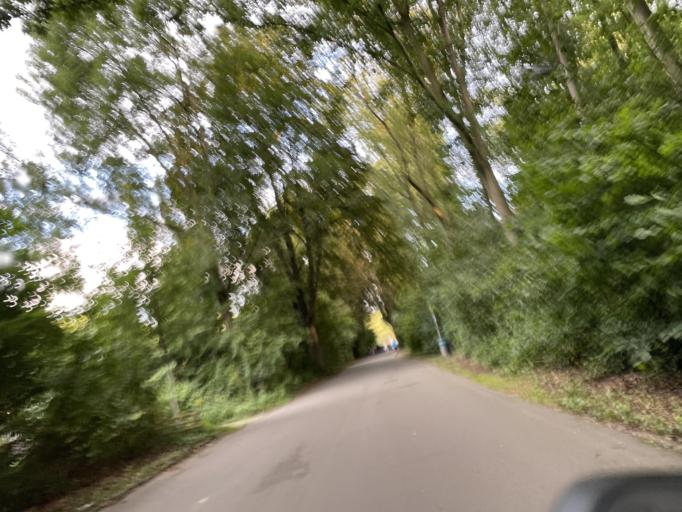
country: DE
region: North Rhine-Westphalia
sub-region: Regierungsbezirk Dusseldorf
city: Velbert
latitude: 51.3993
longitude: 7.0461
